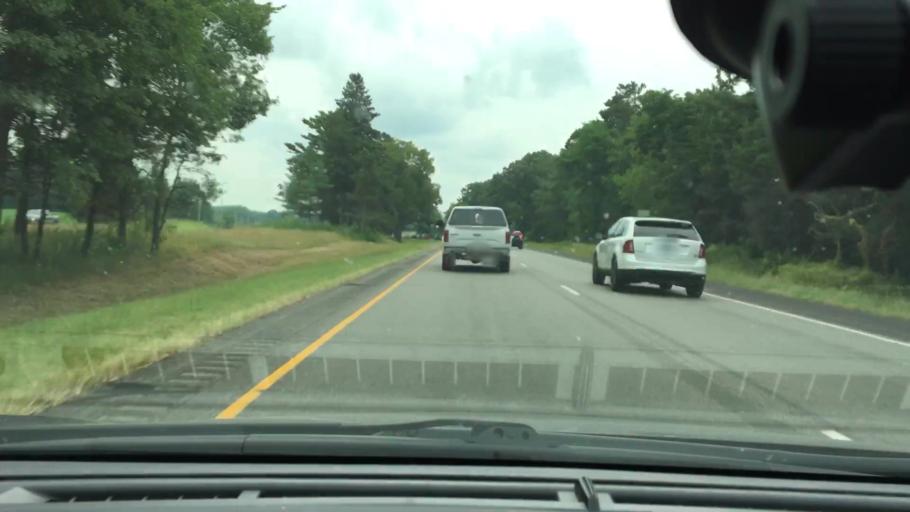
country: US
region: Minnesota
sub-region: Sherburne County
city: Zimmerman
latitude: 45.4949
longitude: -93.5829
